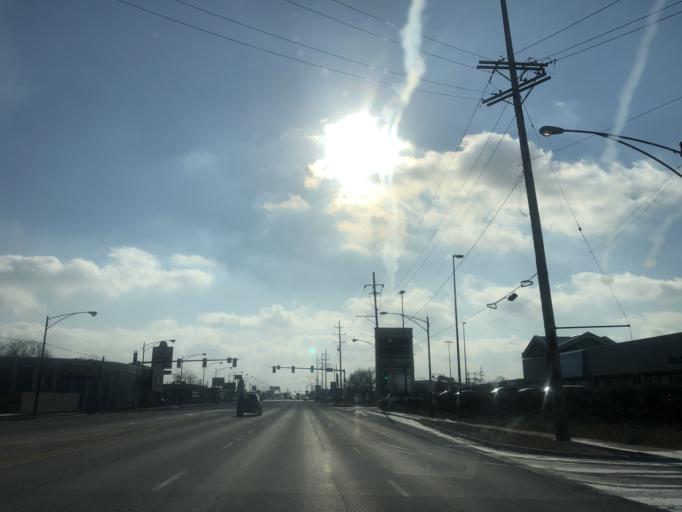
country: US
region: Illinois
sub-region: Cook County
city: Hometown
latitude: 41.7535
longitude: -87.7416
